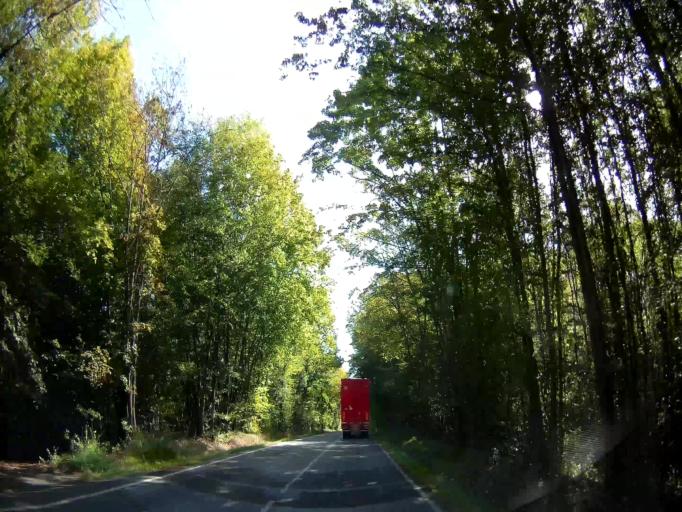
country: BE
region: Wallonia
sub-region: Province de Namur
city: Rochefort
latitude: 50.1676
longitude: 5.1584
